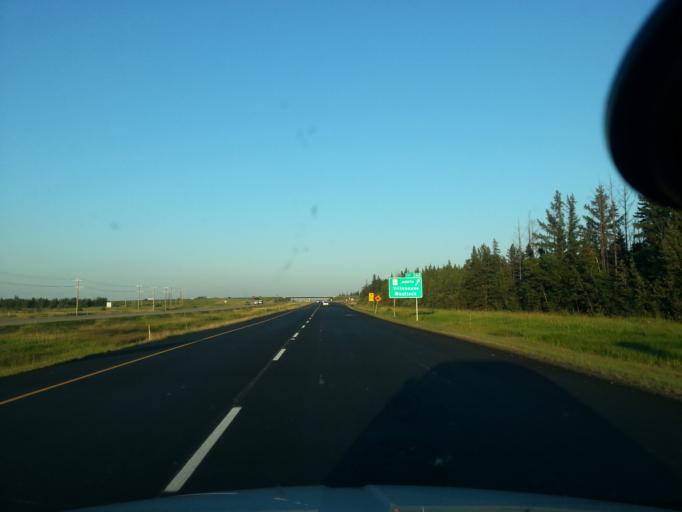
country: CA
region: Alberta
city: Spruce Grove
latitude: 53.5705
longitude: -113.8234
